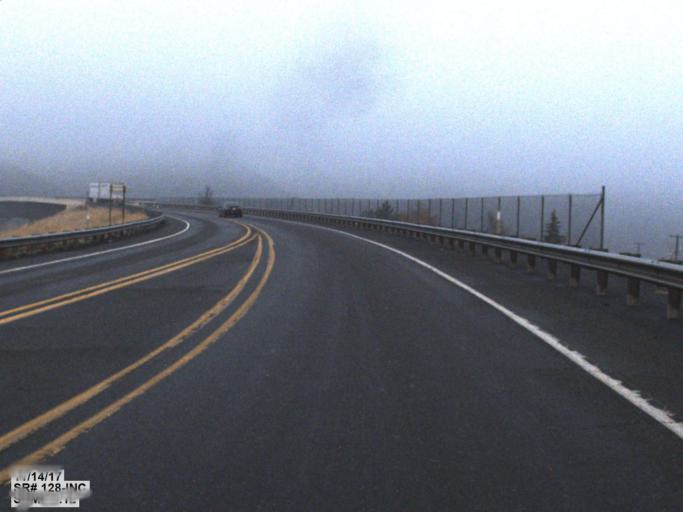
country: US
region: Washington
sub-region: Asotin County
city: West Clarkston-Highland
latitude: 46.4216
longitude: -117.0694
